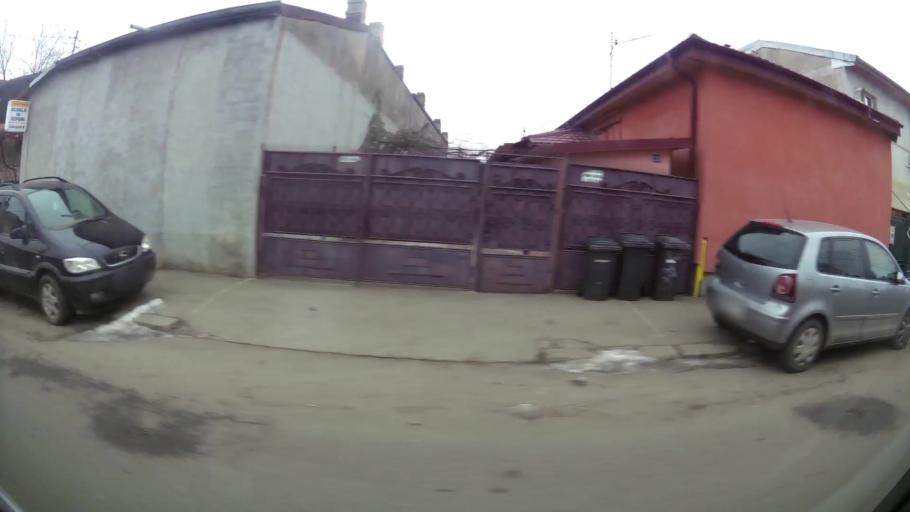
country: RO
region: Prahova
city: Ploiesti
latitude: 44.9443
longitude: 26.0290
